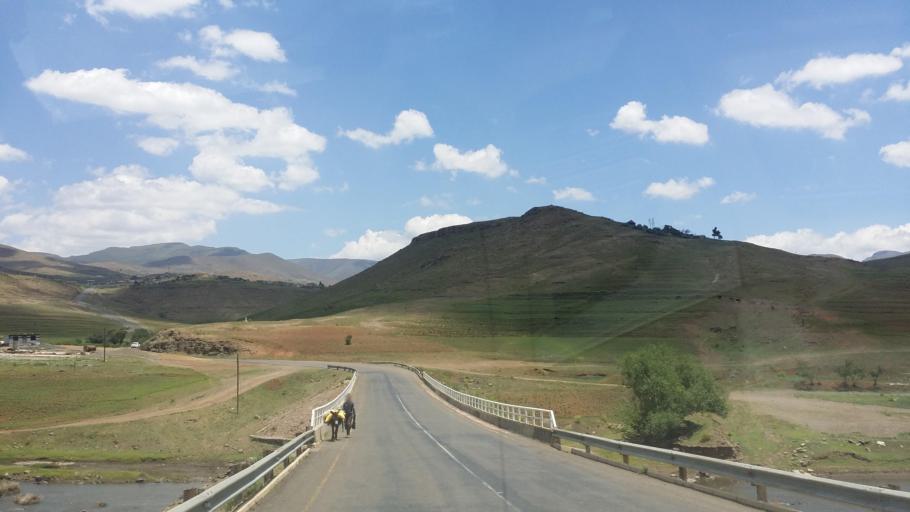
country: LS
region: Mokhotlong
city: Mokhotlong
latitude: -29.2119
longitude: 28.8868
